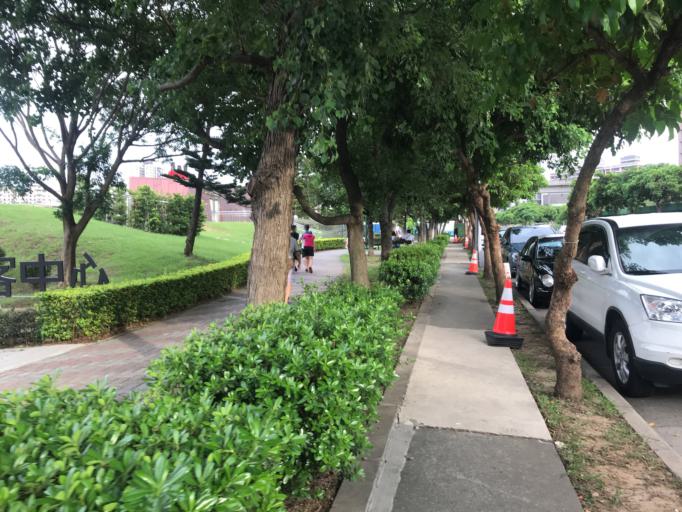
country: TW
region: Taiwan
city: Taoyuan City
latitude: 25.0054
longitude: 121.2040
